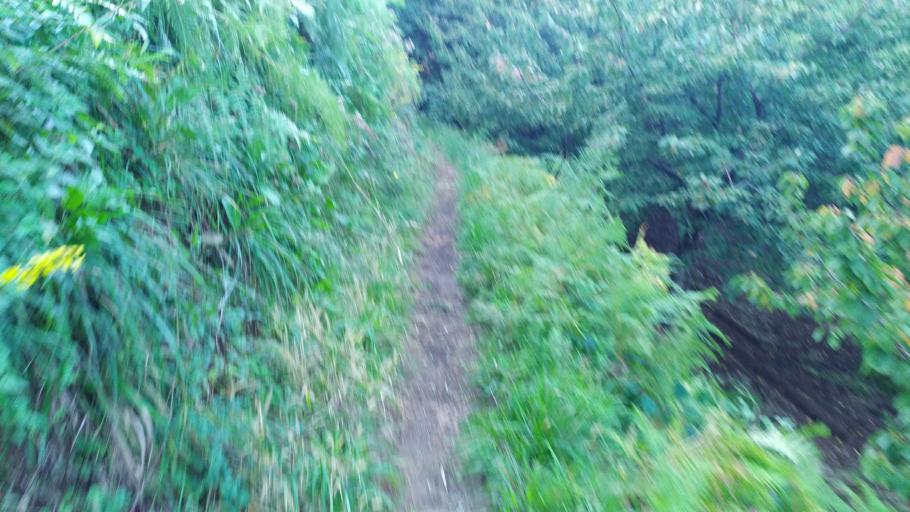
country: IT
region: Campania
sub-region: Provincia di Salerno
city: Nocera Superiore
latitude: 40.7186
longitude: 14.6851
